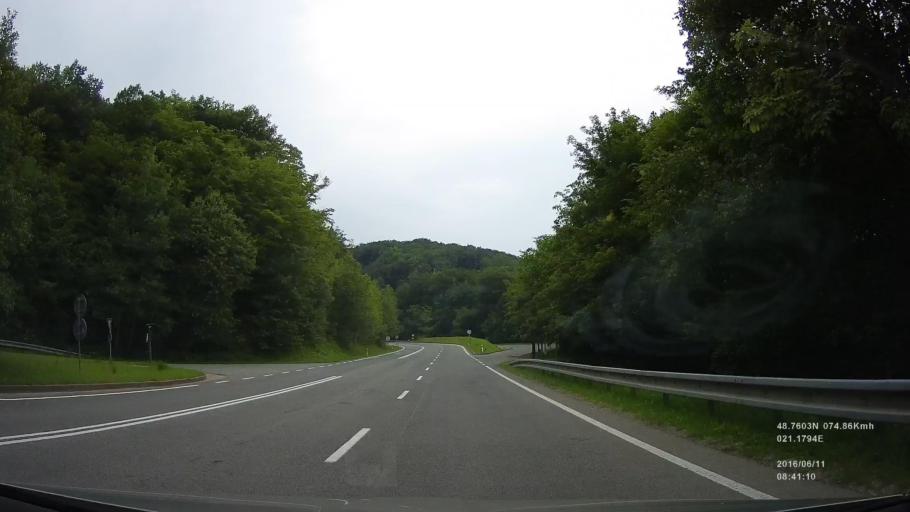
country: SK
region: Kosicky
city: Kosice
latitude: 48.7505
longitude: 21.2265
